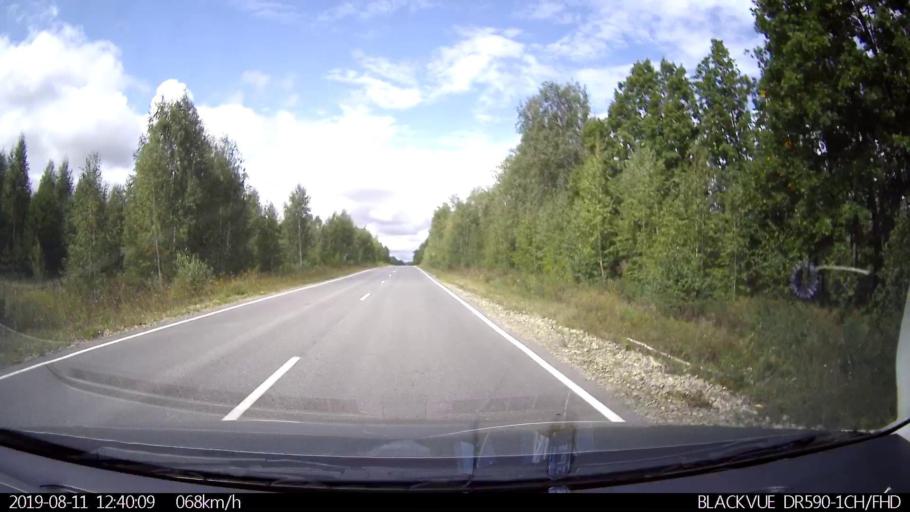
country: RU
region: Ulyanovsk
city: Ignatovka
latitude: 53.8371
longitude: 47.7850
